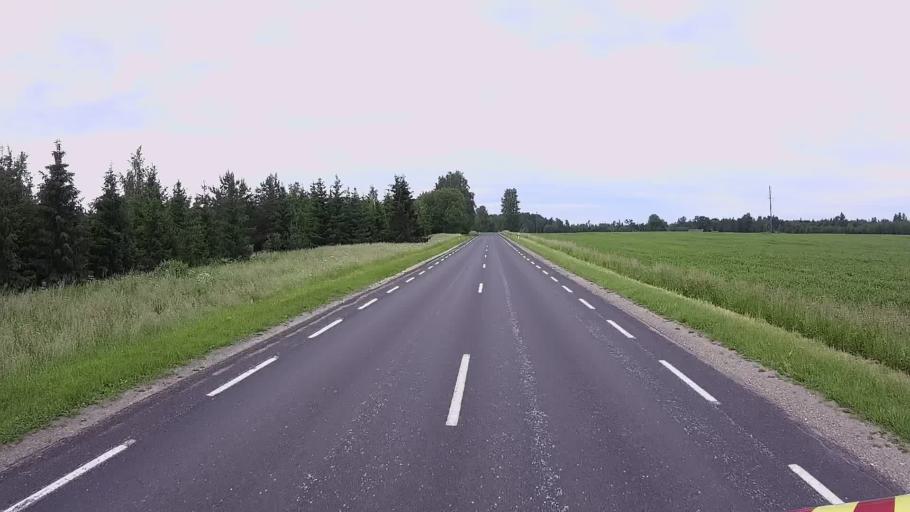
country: EE
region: Viljandimaa
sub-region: Karksi vald
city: Karksi-Nuia
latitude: 58.2009
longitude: 25.6180
